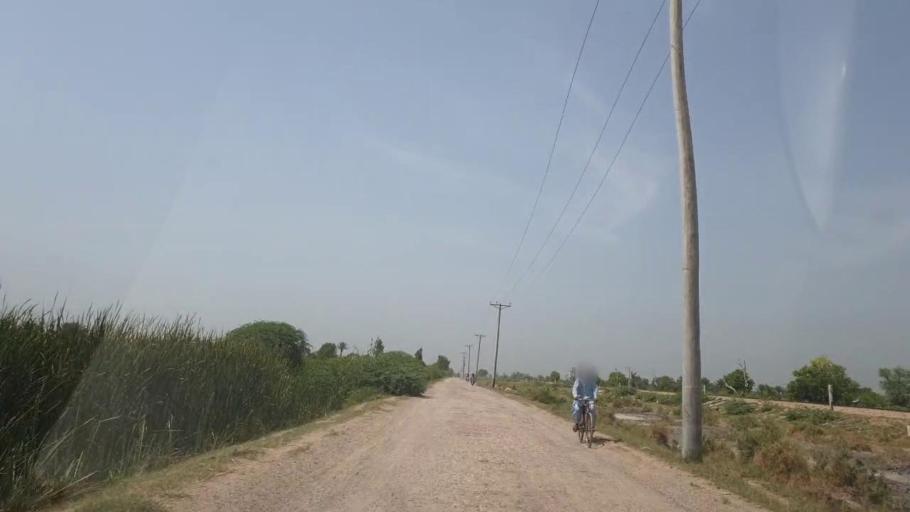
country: PK
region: Sindh
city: Gambat
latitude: 27.3311
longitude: 68.5413
